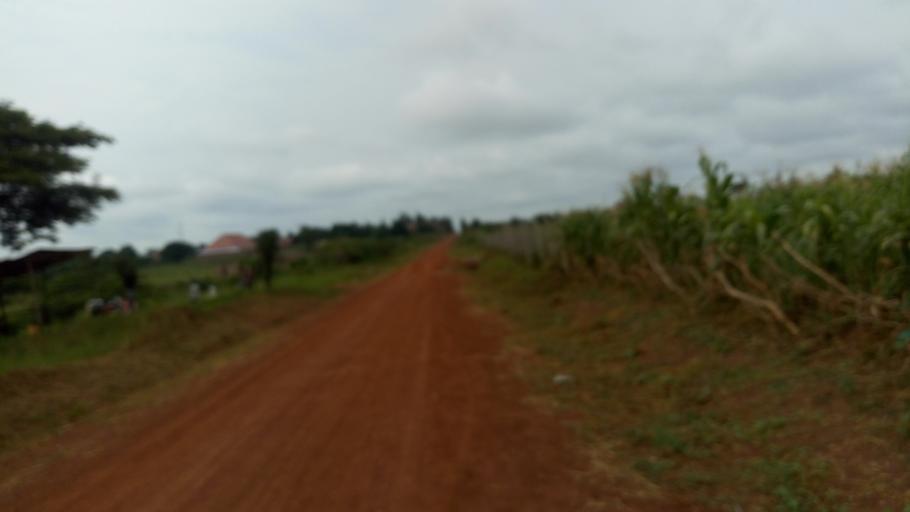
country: UG
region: Western Region
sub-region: Kiryandongo District
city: Kiryandongo
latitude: 1.8073
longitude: 32.0130
